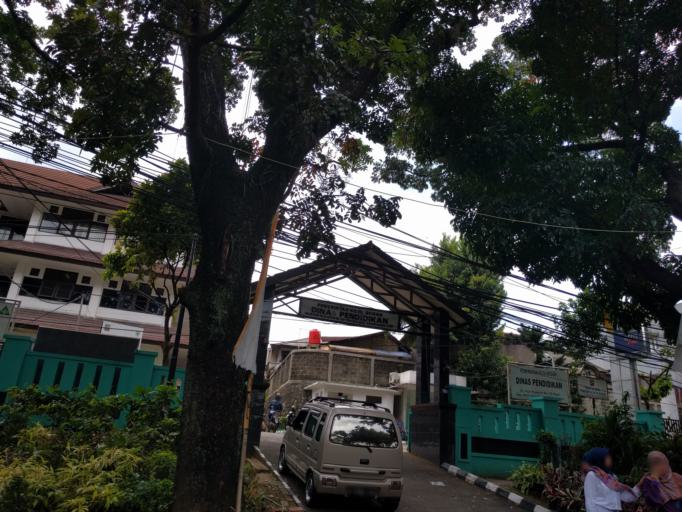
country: ID
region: West Java
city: Bogor
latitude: -6.5733
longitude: 106.8083
